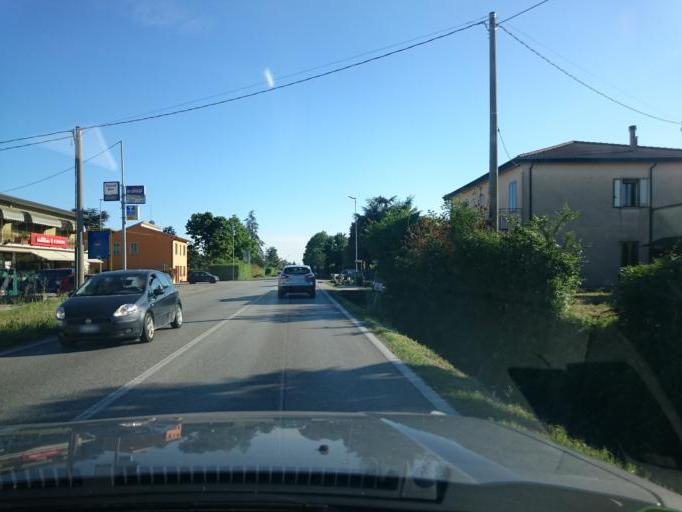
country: IT
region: Veneto
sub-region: Provincia di Venezia
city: Caselle
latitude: 45.4784
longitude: 12.0014
